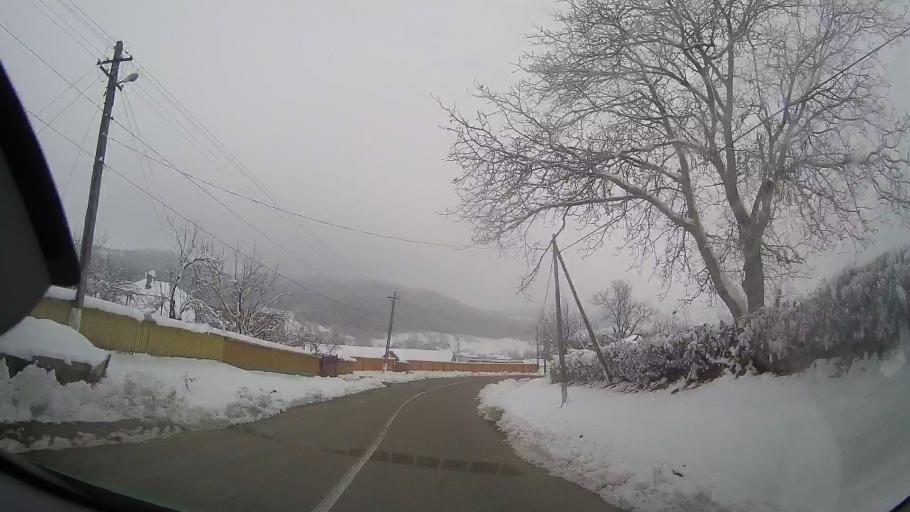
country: RO
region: Neamt
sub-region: Comuna Bozieni
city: Bozieni
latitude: 46.8365
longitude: 27.1656
